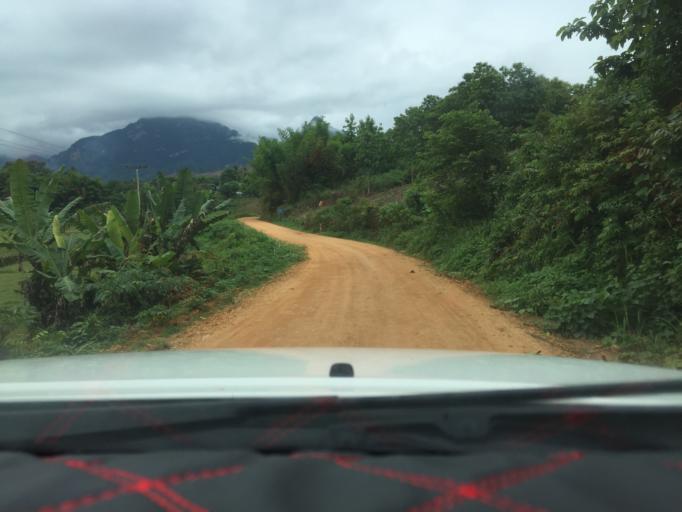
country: TH
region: Phayao
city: Phu Sang
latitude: 19.7718
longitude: 100.5289
